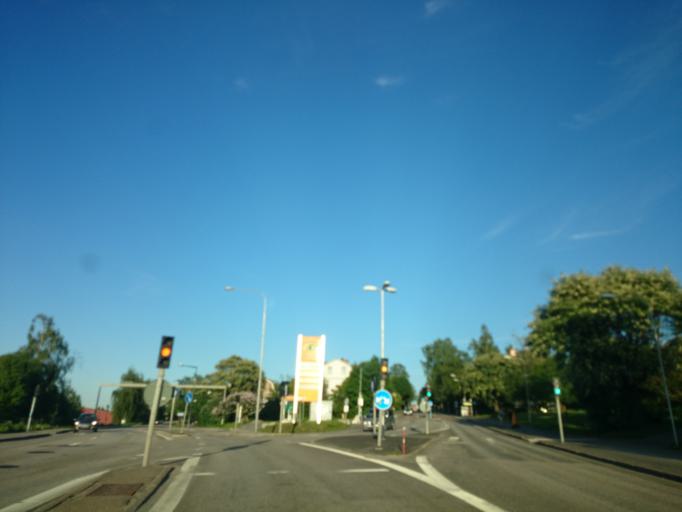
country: SE
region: Vaesternorrland
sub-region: Sundsvalls Kommun
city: Sundsvall
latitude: 62.3850
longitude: 17.3129
